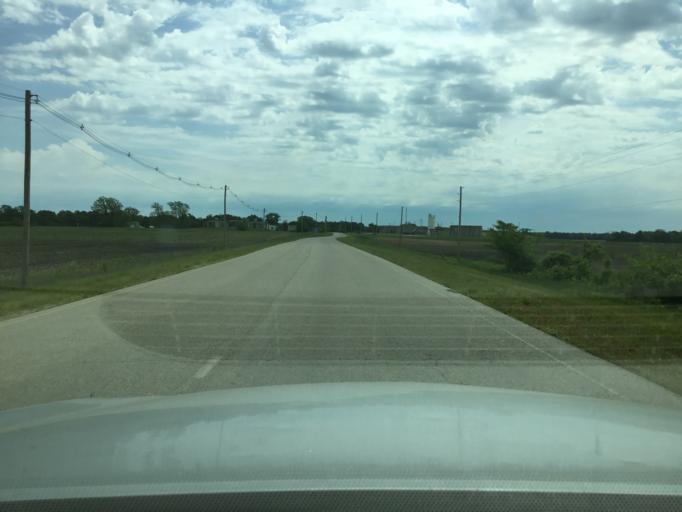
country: US
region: Kansas
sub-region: Montgomery County
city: Coffeyville
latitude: 37.0072
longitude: -95.6139
